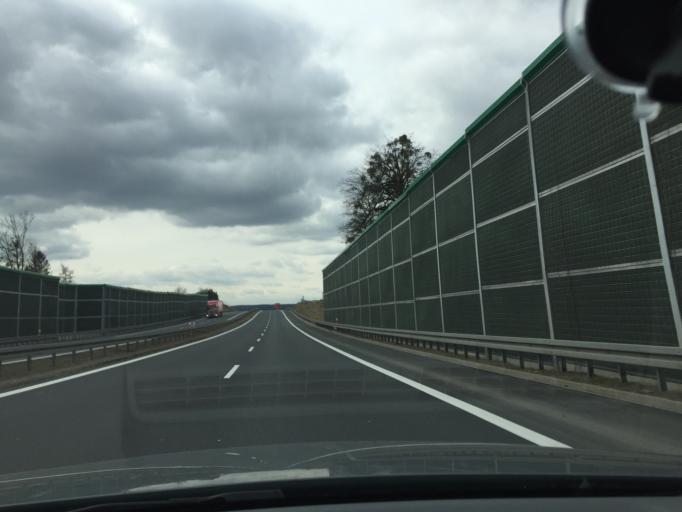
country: PL
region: Silesian Voivodeship
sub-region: Powiat cieszynski
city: Skoczow
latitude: 49.7874
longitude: 18.7612
